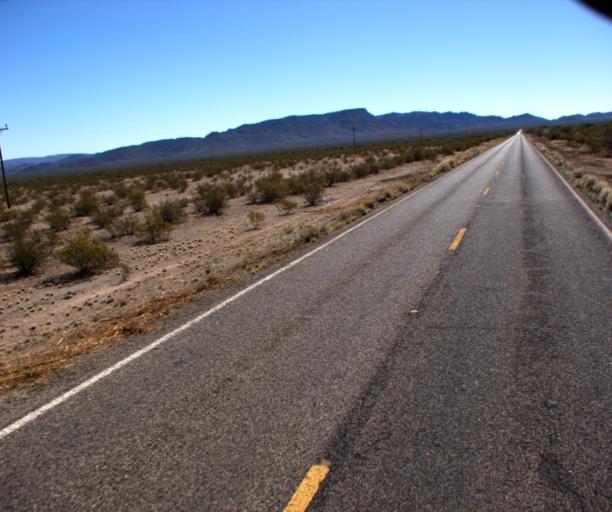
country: US
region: Arizona
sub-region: Pima County
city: Ajo
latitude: 32.3388
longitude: -112.7978
